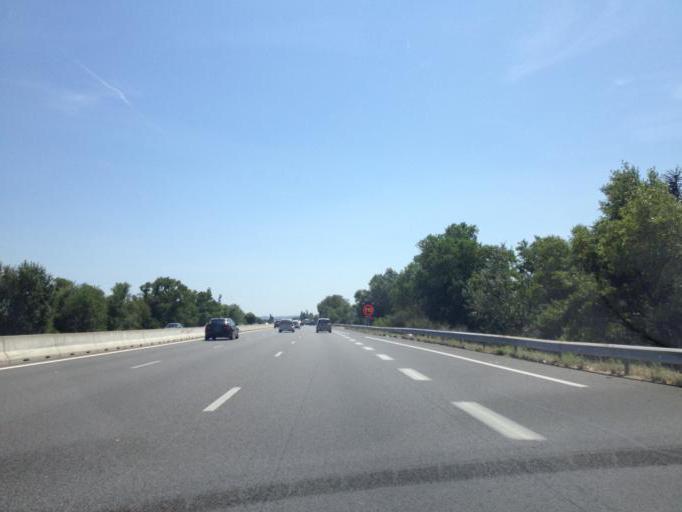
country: FR
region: Rhone-Alpes
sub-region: Departement de la Drome
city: La Garde-Adhemar
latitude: 44.3998
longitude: 4.7287
